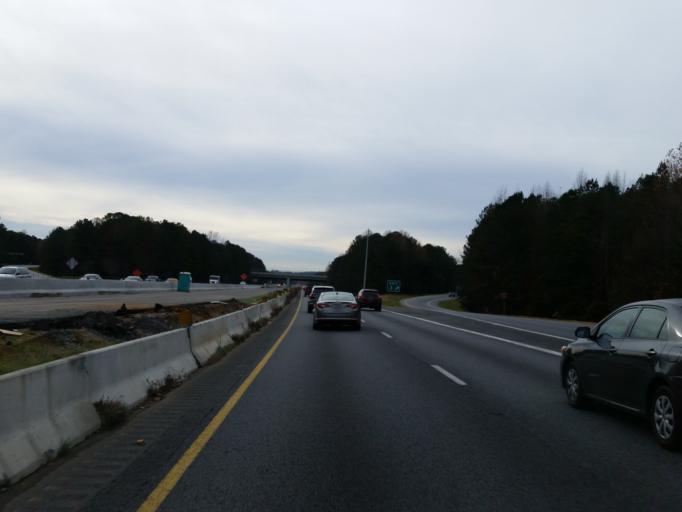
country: US
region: Georgia
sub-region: Cobb County
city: Kennesaw
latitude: 34.0424
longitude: -84.5636
